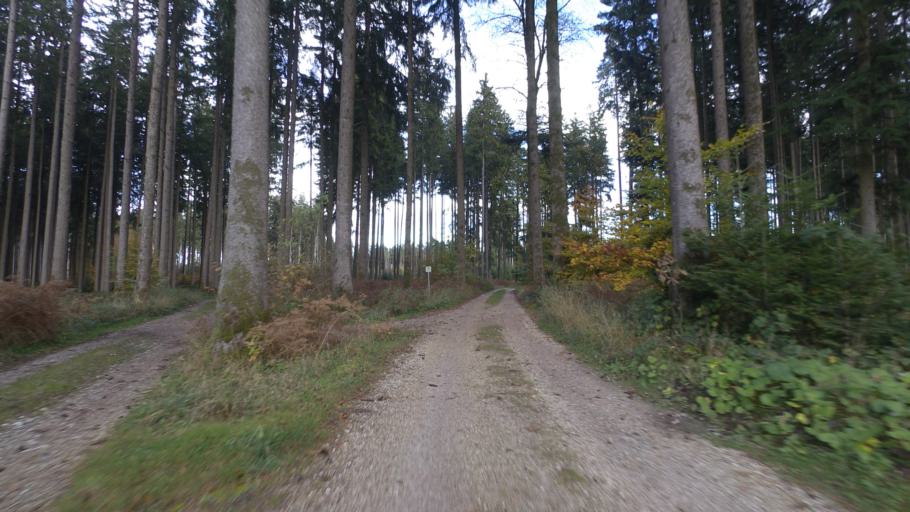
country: DE
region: Bavaria
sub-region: Upper Bavaria
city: Traunreut
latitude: 47.9333
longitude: 12.5789
